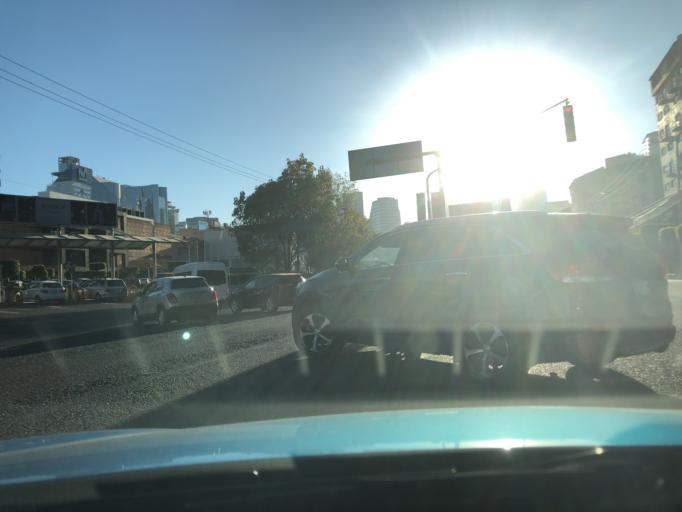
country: MX
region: Mexico City
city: Col. Bosques de las Lomas
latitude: 19.3644
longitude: -99.2706
